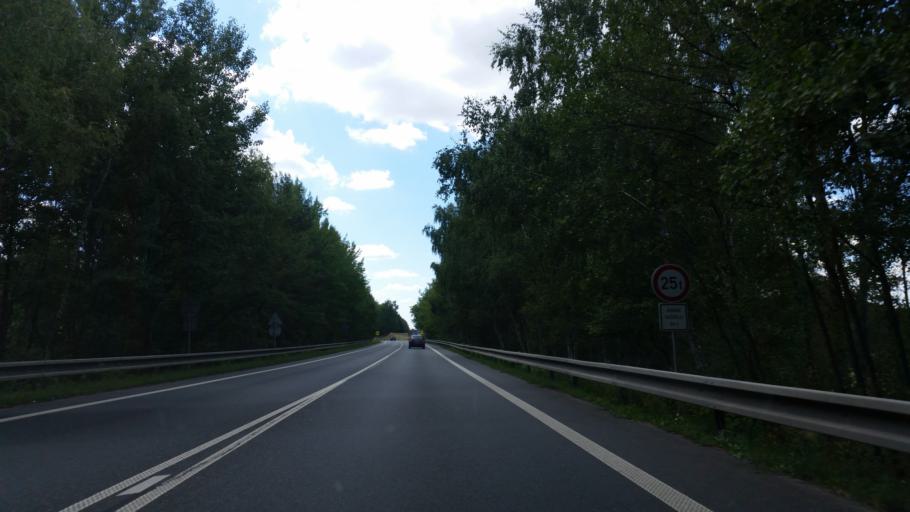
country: CZ
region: Vysocina
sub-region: Okres Pelhrimov
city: Humpolec
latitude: 49.5106
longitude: 15.3398
